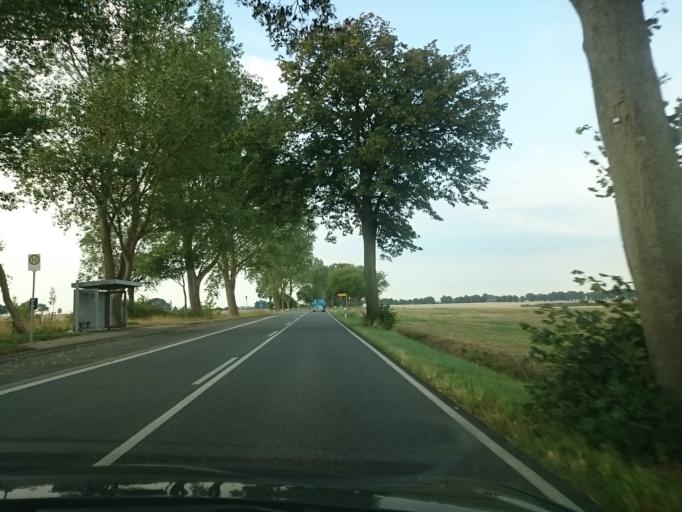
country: DE
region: Mecklenburg-Vorpommern
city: Borrentin
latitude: 53.8323
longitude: 12.9890
